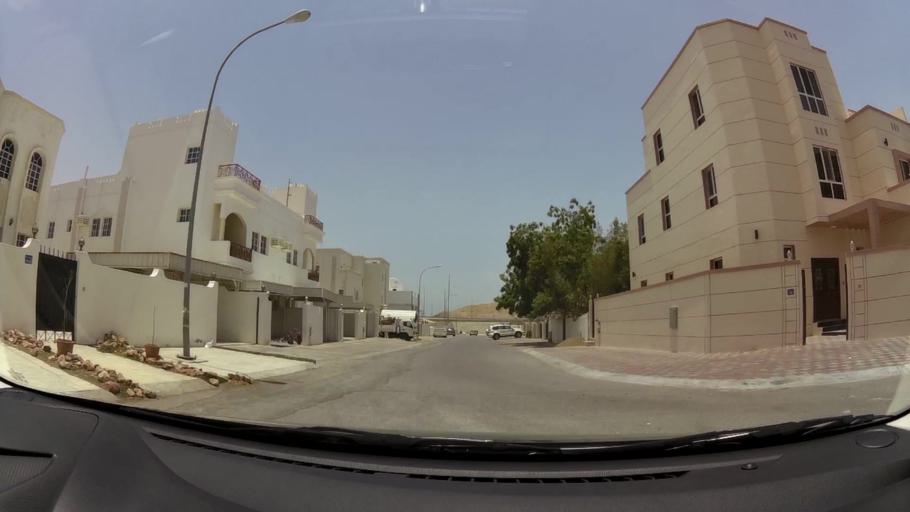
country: OM
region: Muhafazat Masqat
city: Bawshar
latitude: 23.5692
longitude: 58.4278
